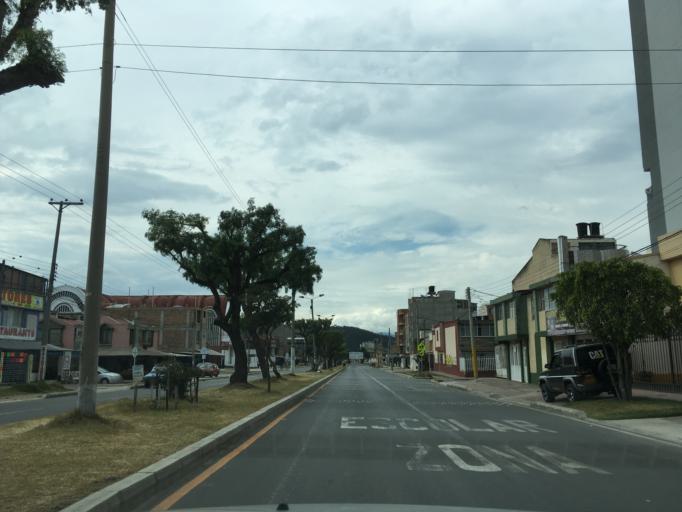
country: CO
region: Boyaca
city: Sogamoso
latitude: 5.7124
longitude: -72.9341
